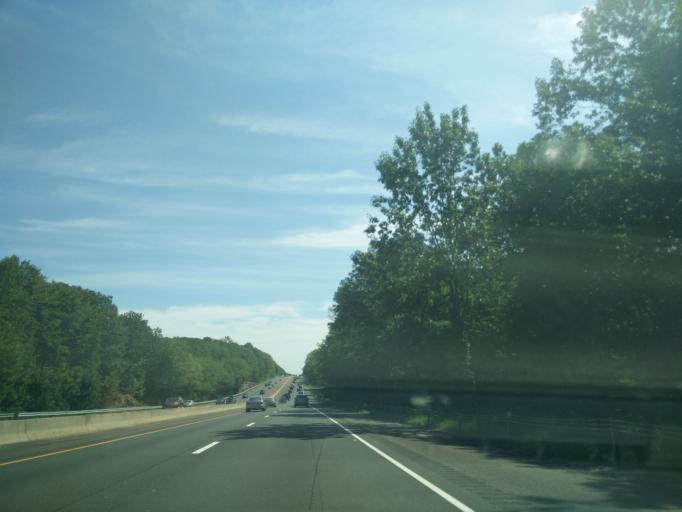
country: US
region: Connecticut
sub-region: New Haven County
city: North Branford
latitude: 41.2969
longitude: -72.7479
